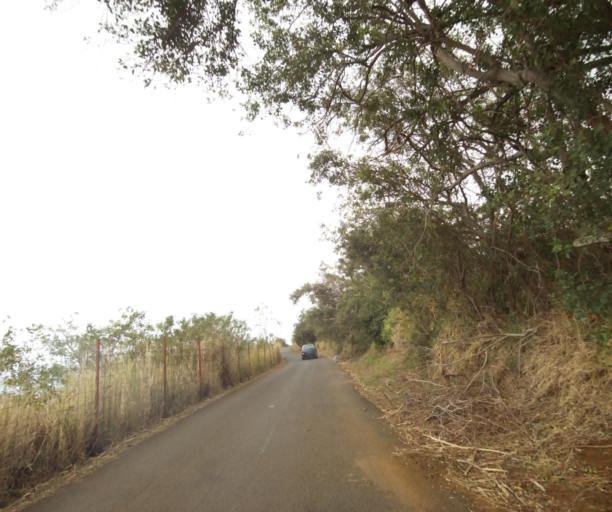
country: RE
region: Reunion
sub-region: Reunion
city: Saint-Paul
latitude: -21.0275
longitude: 55.3011
